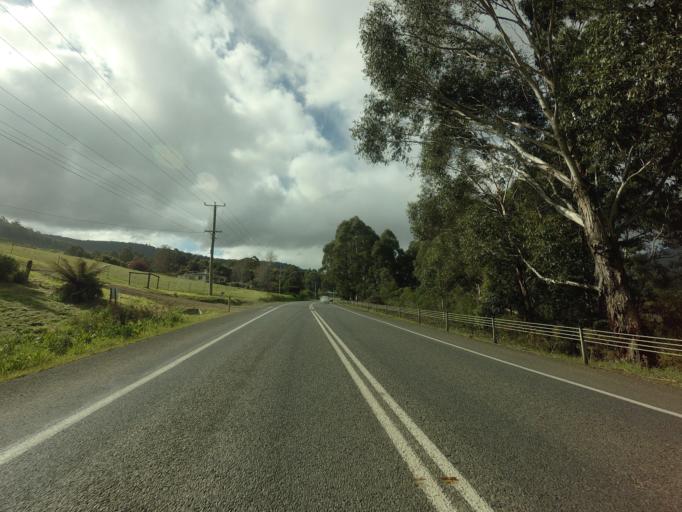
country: AU
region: Tasmania
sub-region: Huon Valley
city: Franklin
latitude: -43.0647
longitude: 147.0253
